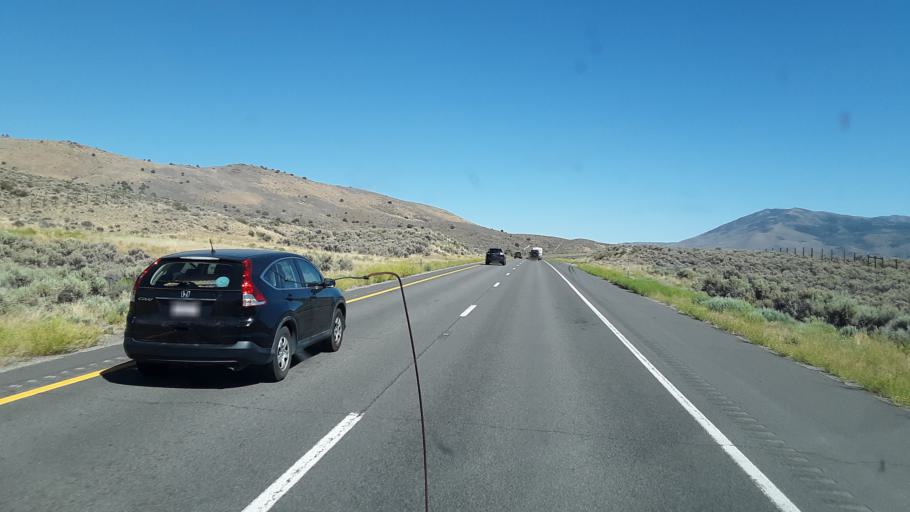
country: US
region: Nevada
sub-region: Washoe County
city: Cold Springs
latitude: 39.6949
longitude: -120.0237
